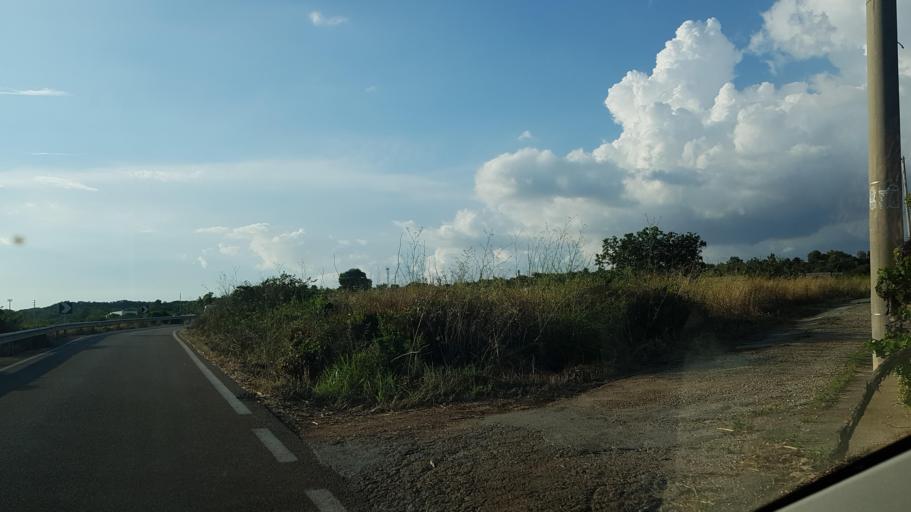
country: IT
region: Apulia
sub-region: Provincia di Lecce
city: Gemini
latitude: 39.8541
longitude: 18.2062
